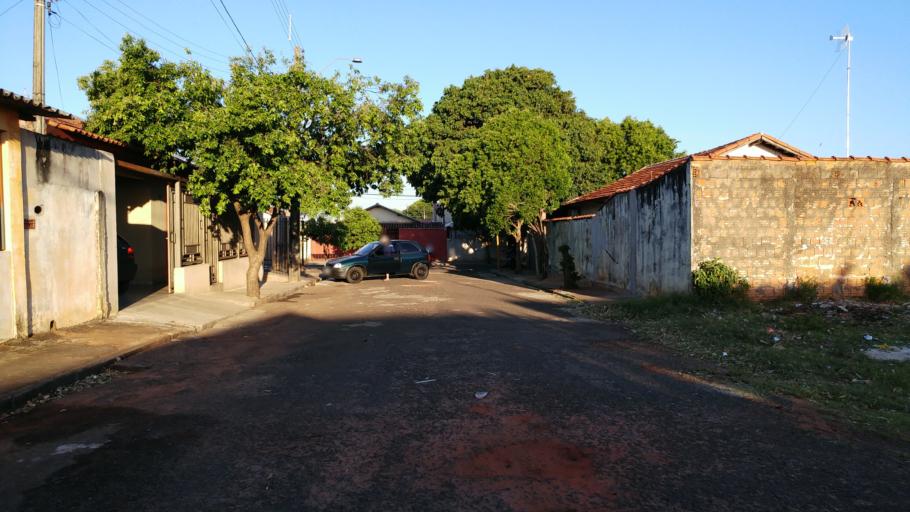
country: BR
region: Sao Paulo
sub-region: Paraguacu Paulista
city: Paraguacu Paulista
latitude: -22.4332
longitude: -50.5837
